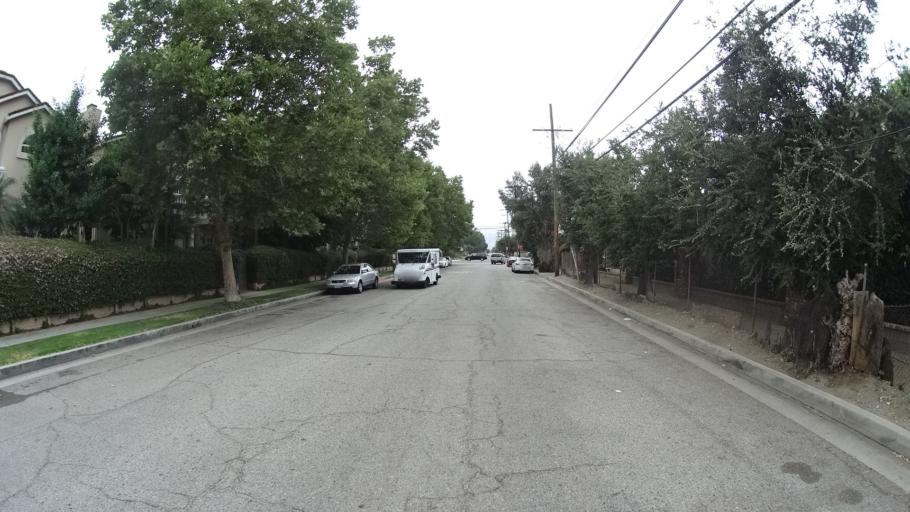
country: US
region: California
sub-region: Los Angeles County
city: San Fernando
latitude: 34.2418
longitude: -118.4588
